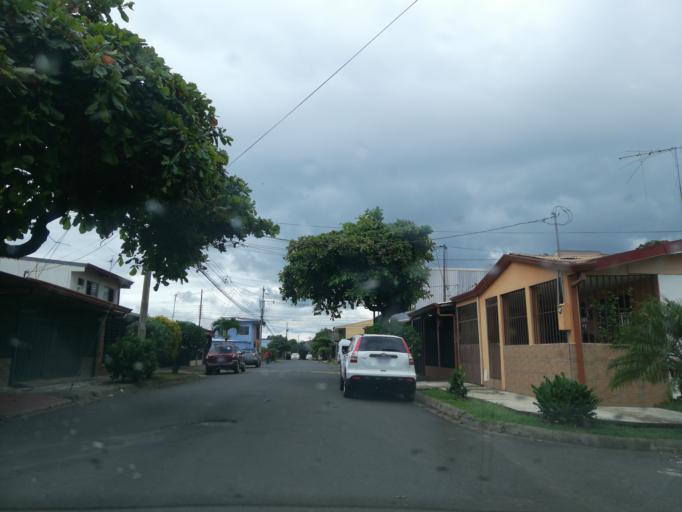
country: CR
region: Alajuela
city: Alajuela
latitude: 10.0309
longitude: -84.2013
